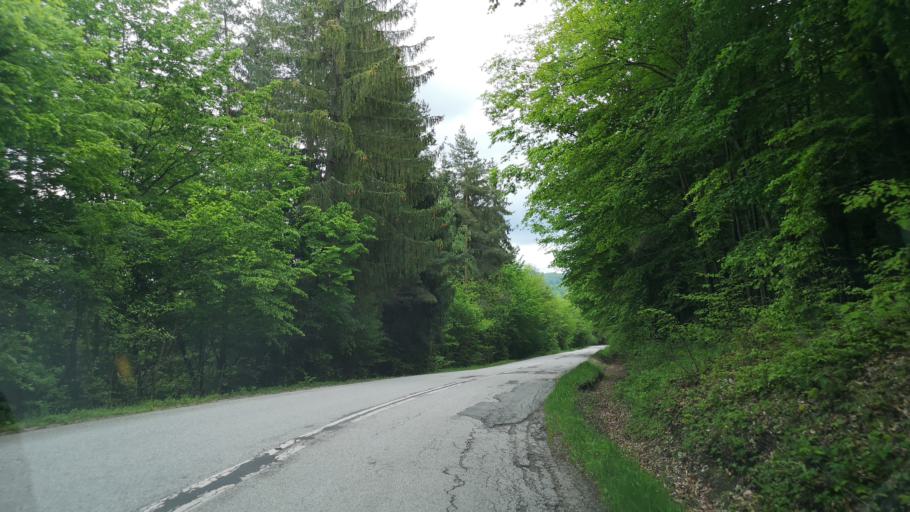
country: SK
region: Kosicky
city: Dobsina
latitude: 48.7199
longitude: 20.3985
